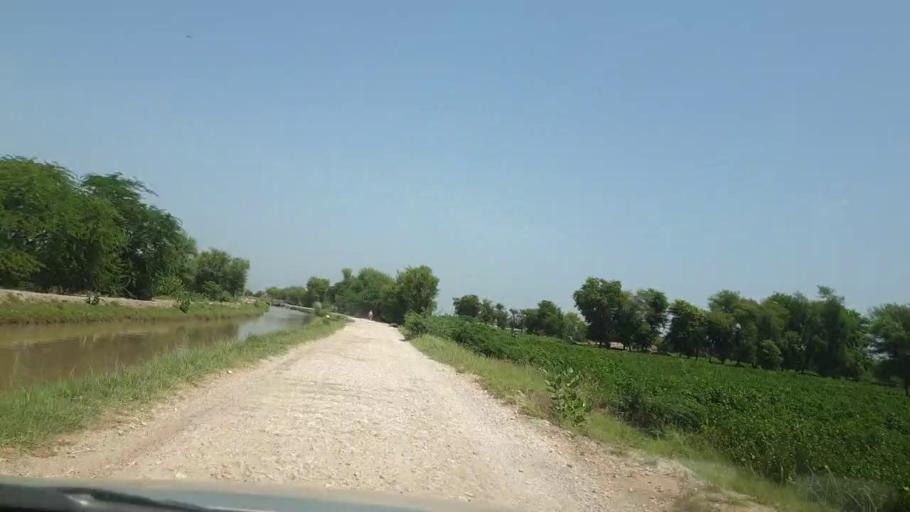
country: PK
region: Sindh
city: Pano Aqil
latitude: 27.6481
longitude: 69.1056
